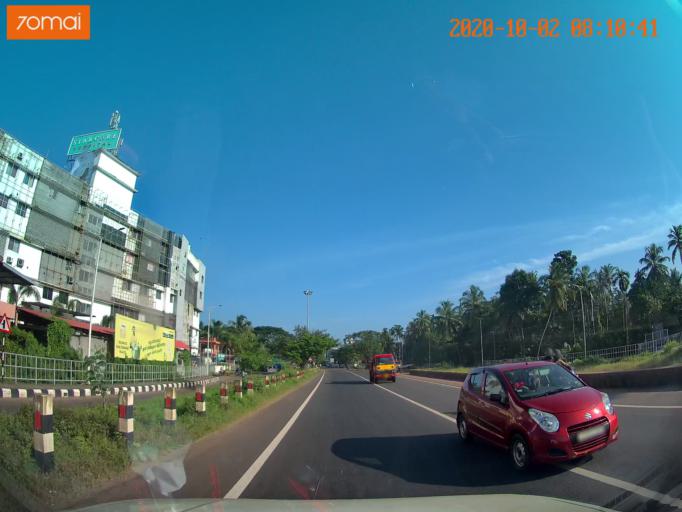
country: IN
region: Kerala
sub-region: Kozhikode
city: Kozhikode
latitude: 11.2688
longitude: 75.8099
